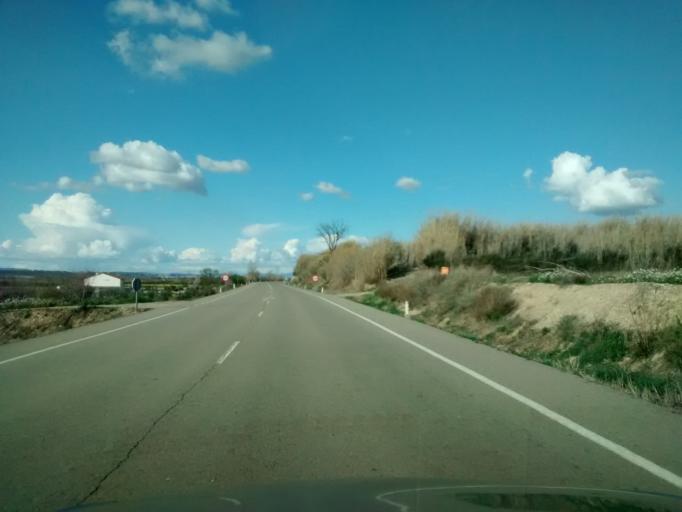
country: ES
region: Aragon
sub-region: Provincia de Zaragoza
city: Villanueva de Gallego
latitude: 41.7764
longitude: -0.7895
